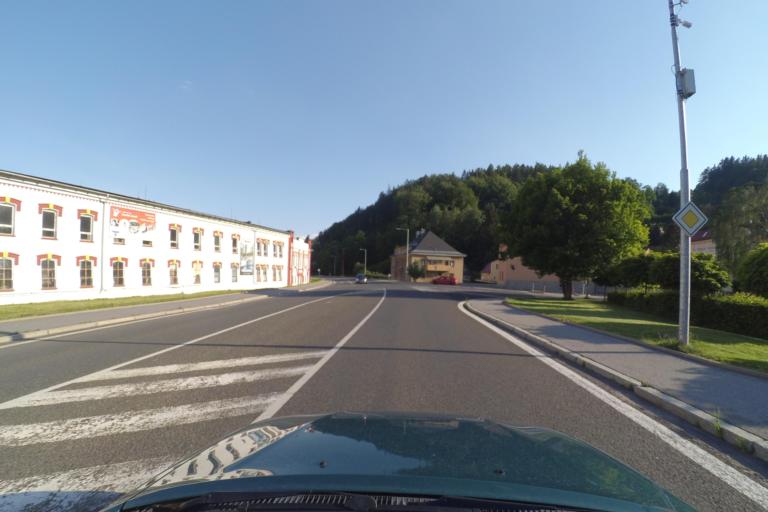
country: CZ
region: Kralovehradecky
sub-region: Okres Trutnov
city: Svoboda nad Upou
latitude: 50.6329
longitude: 15.8119
